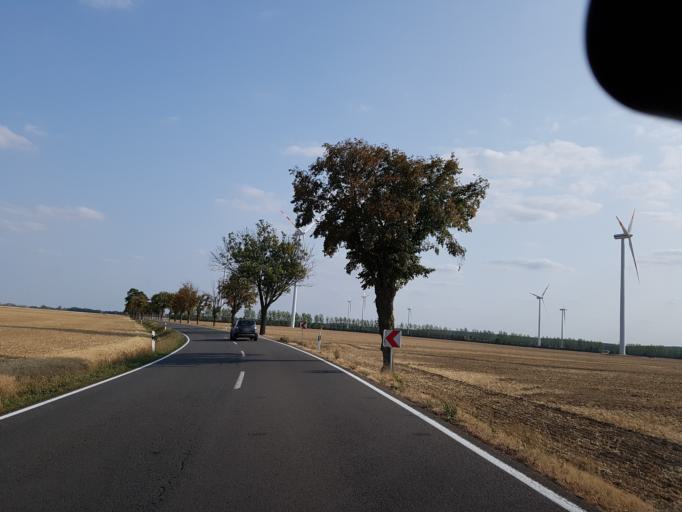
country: DE
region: Saxony-Anhalt
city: Muhlanger
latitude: 51.7765
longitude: 12.7223
